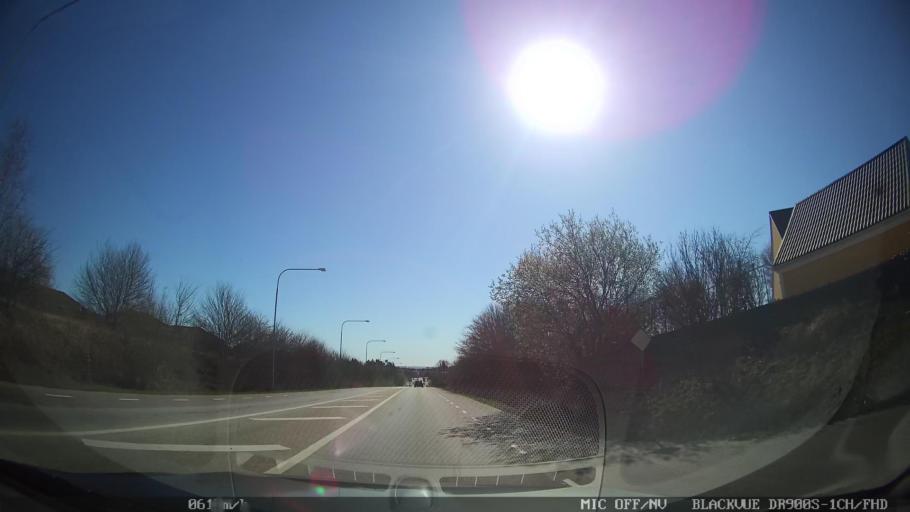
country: SE
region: Skane
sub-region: Ystads Kommun
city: Ystad
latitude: 55.4361
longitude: 13.7964
